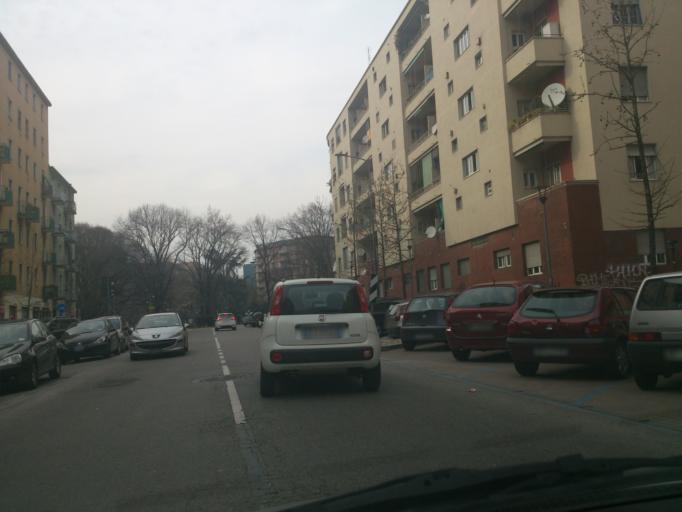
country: IT
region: Lombardy
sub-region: Citta metropolitana di Milano
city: Milano
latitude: 45.4519
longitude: 9.2225
